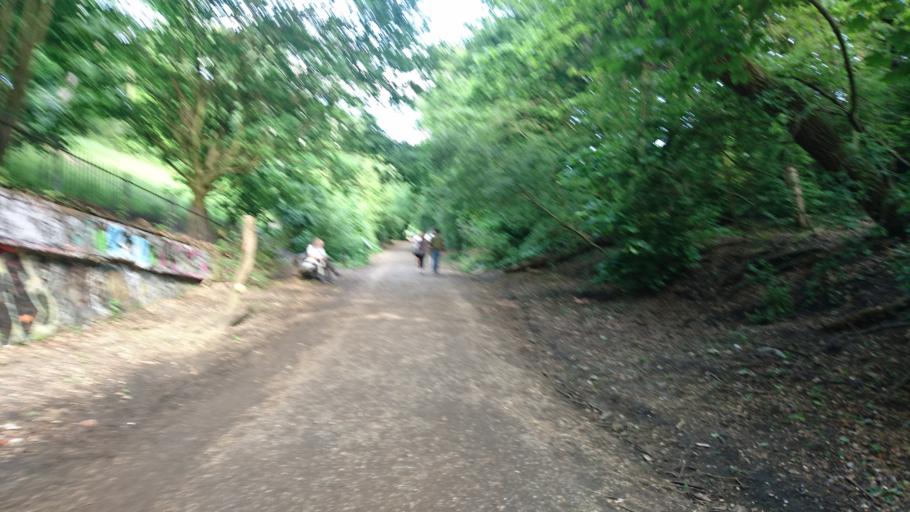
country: GB
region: England
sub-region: Greater London
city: Crouch End
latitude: 51.5740
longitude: -0.1195
